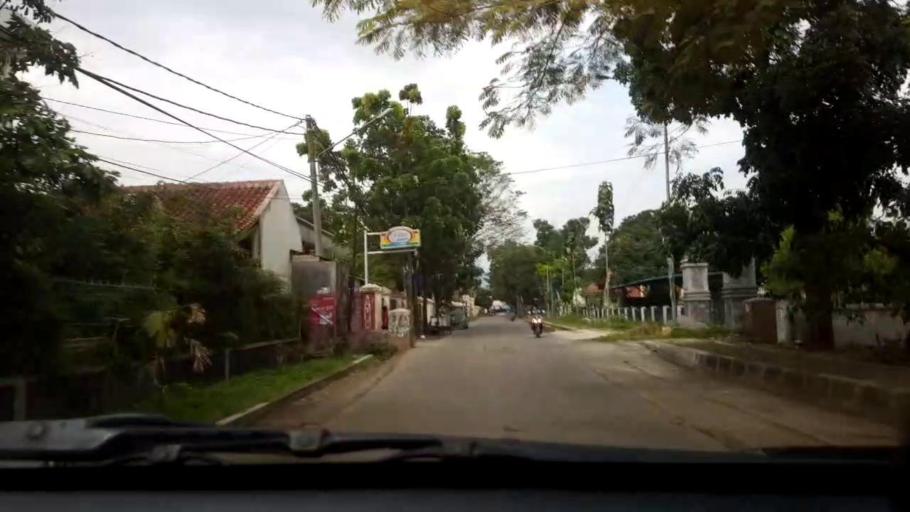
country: ID
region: West Java
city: Cileunyi
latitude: -6.9404
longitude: 107.7233
